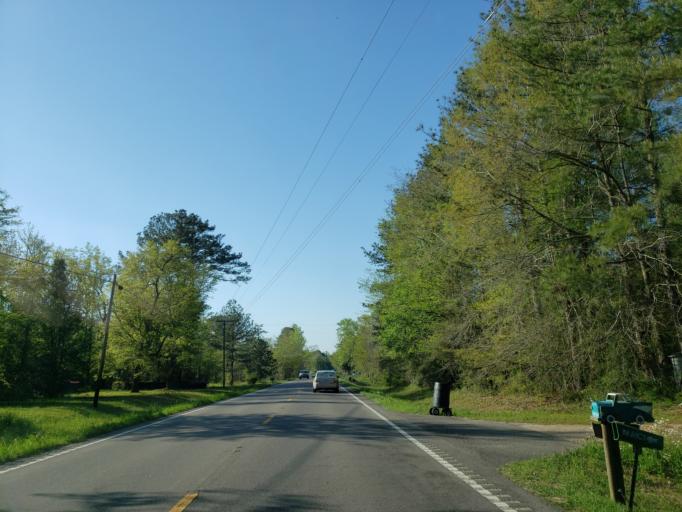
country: US
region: Mississippi
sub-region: Jones County
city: Laurel
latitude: 31.6216
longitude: -89.0868
